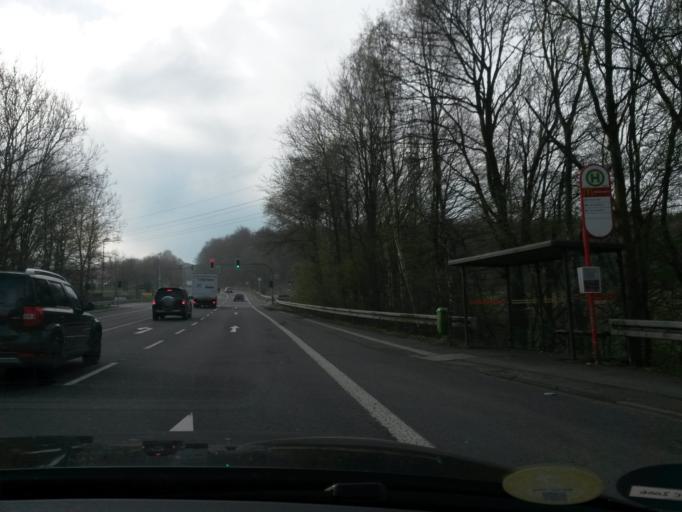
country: DE
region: North Rhine-Westphalia
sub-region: Regierungsbezirk Arnsberg
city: Luedenscheid
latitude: 51.2396
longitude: 7.6057
